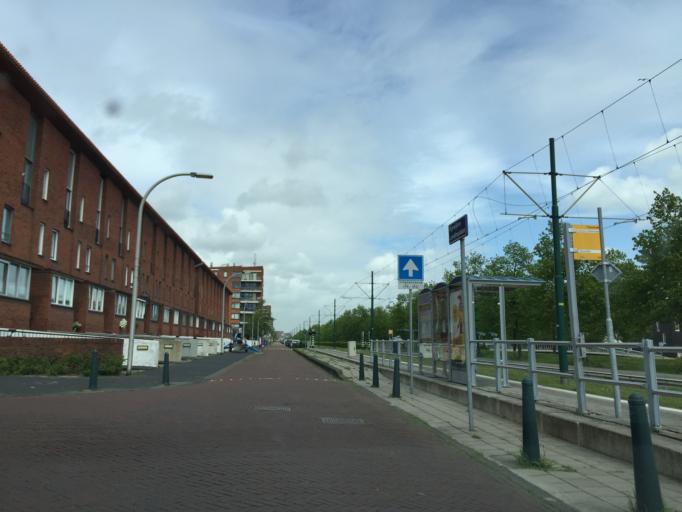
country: NL
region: South Holland
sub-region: Gemeente Den Haag
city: Ypenburg
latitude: 52.0354
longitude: 4.3628
